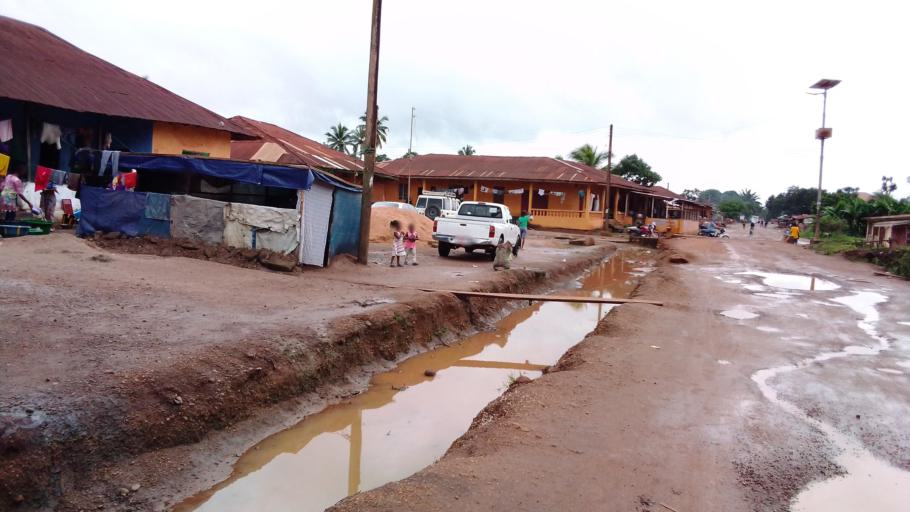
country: SL
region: Eastern Province
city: Kenema
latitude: 7.8698
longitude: -11.1933
